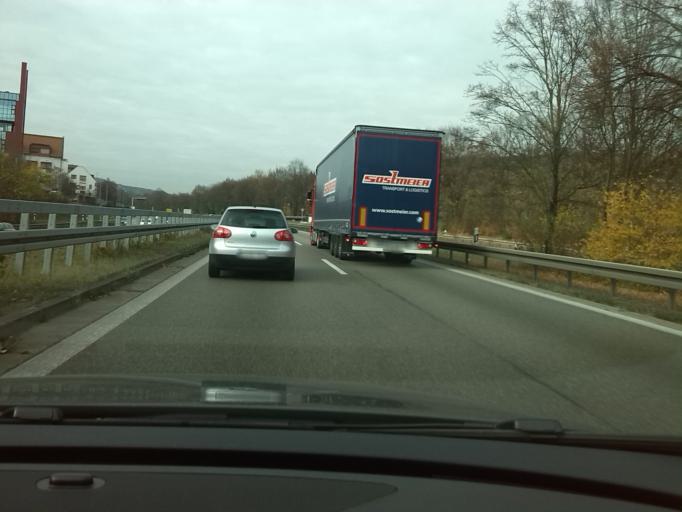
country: DE
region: Baden-Wuerttemberg
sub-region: Regierungsbezirk Stuttgart
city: Esslingen
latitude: 48.7368
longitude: 9.3015
